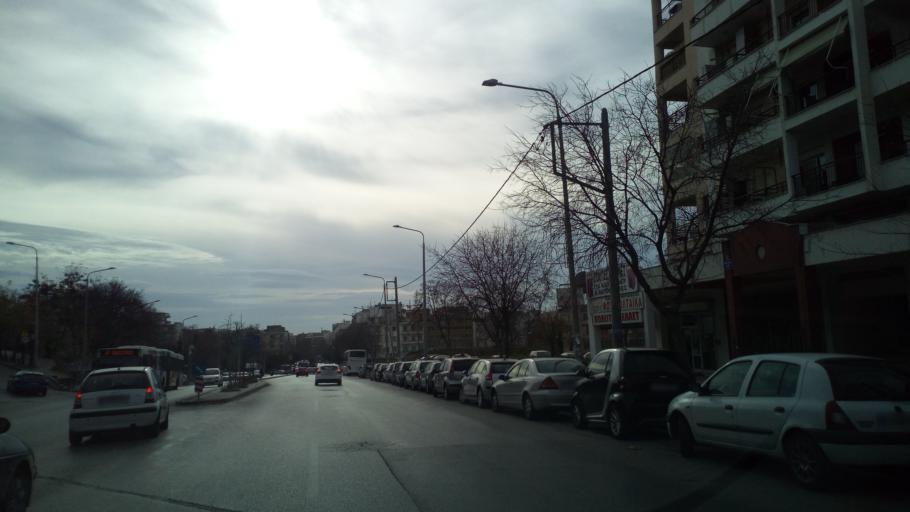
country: GR
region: Central Macedonia
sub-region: Nomos Thessalonikis
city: Thessaloniki
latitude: 40.6467
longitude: 22.9353
